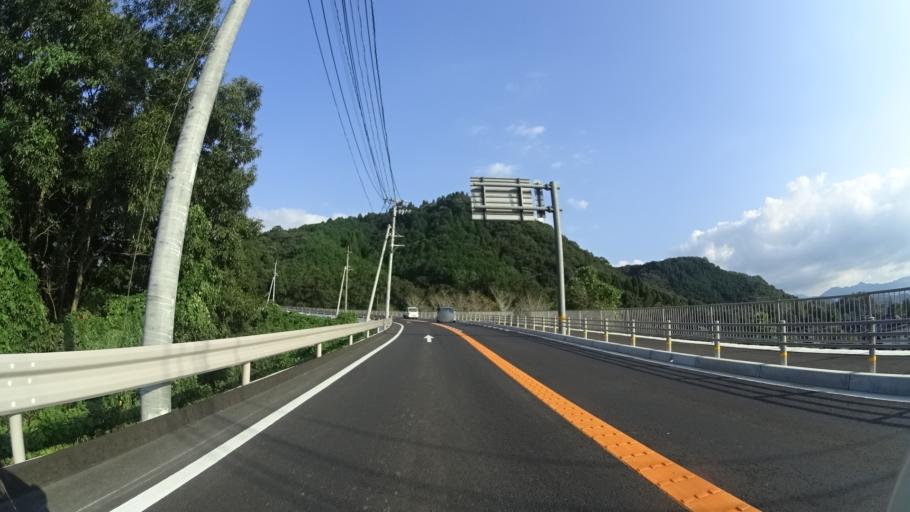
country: JP
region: Oita
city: Bungo-Takada-shi
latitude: 33.4463
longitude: 131.3335
